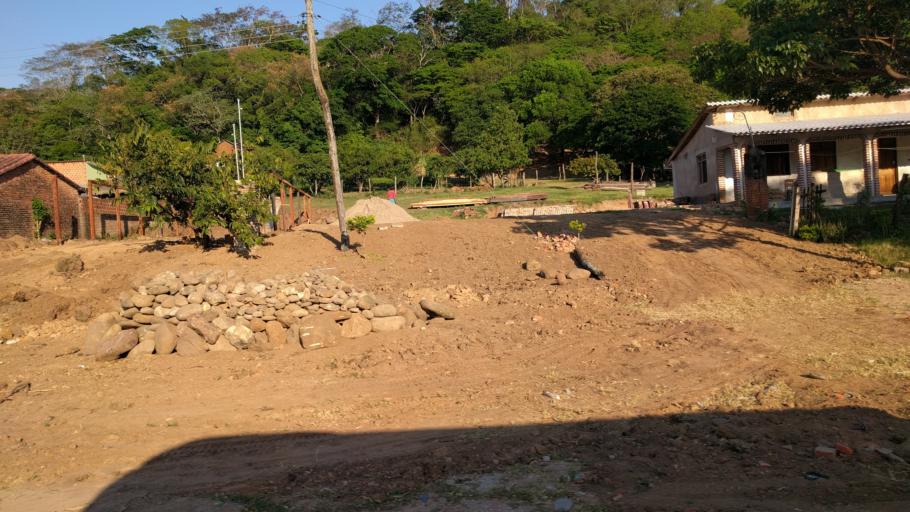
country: BO
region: Santa Cruz
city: Limoncito
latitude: -18.0193
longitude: -63.3975
